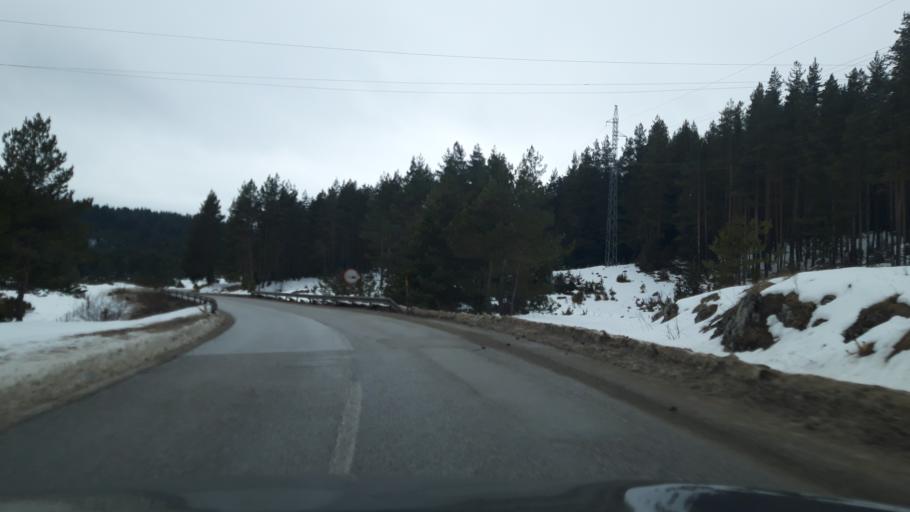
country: BA
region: Republika Srpska
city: Sokolac
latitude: 43.9097
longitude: 18.7056
